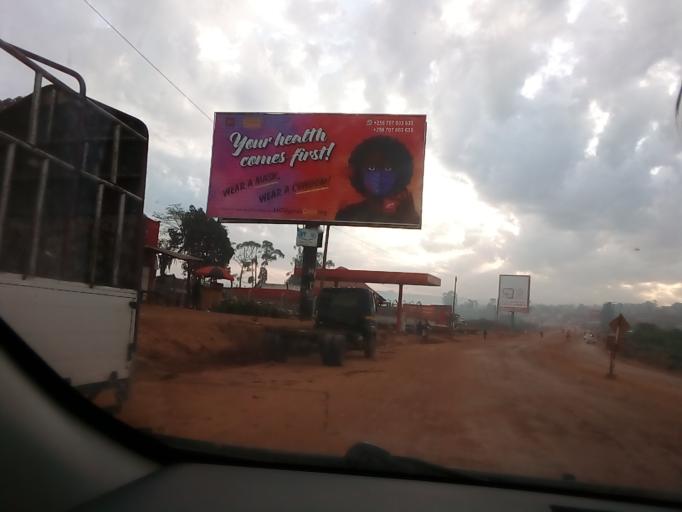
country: UG
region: Central Region
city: Masaka
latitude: -0.3293
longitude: 31.7471
